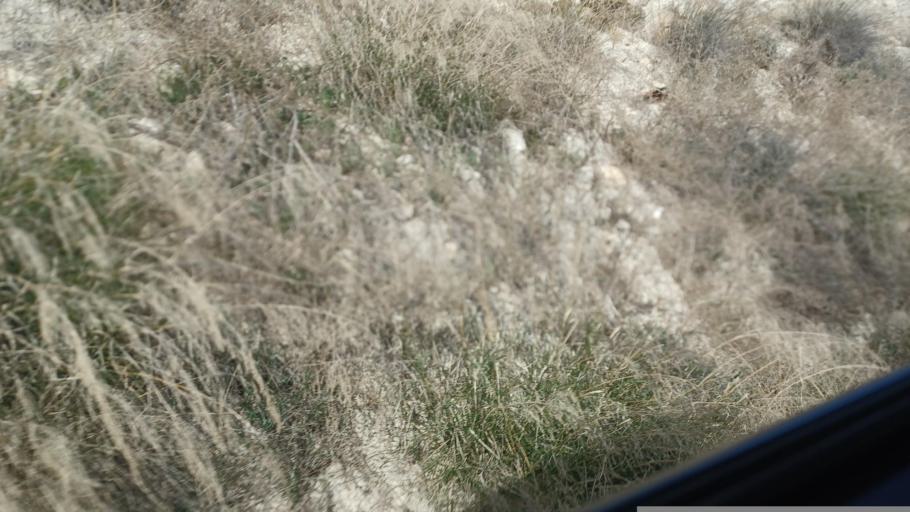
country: CY
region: Limassol
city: Pano Polemidia
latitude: 34.7869
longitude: 32.9823
